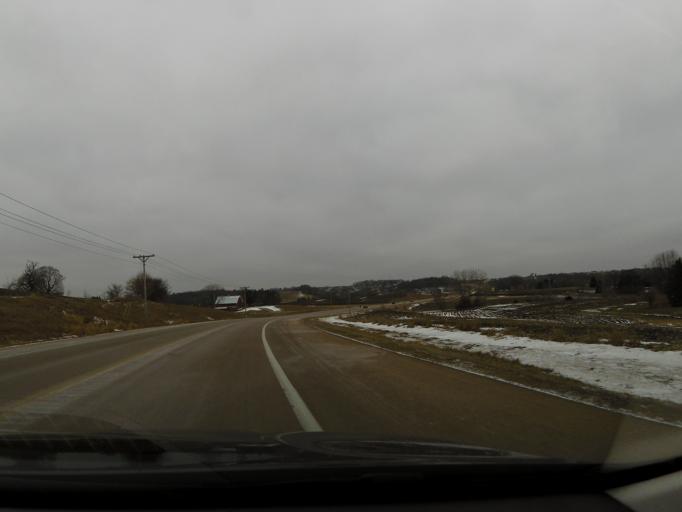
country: US
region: Minnesota
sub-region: Carver County
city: Waconia
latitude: 44.8294
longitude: -93.7558
